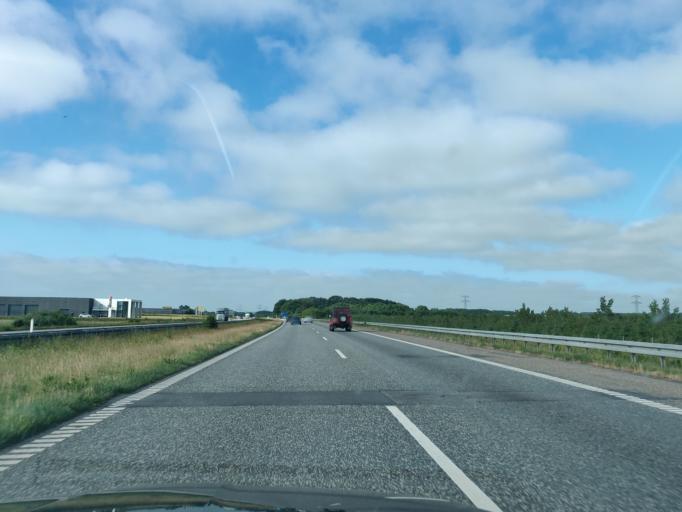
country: DK
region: North Denmark
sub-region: Rebild Kommune
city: Stovring
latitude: 56.8919
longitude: 9.8135
